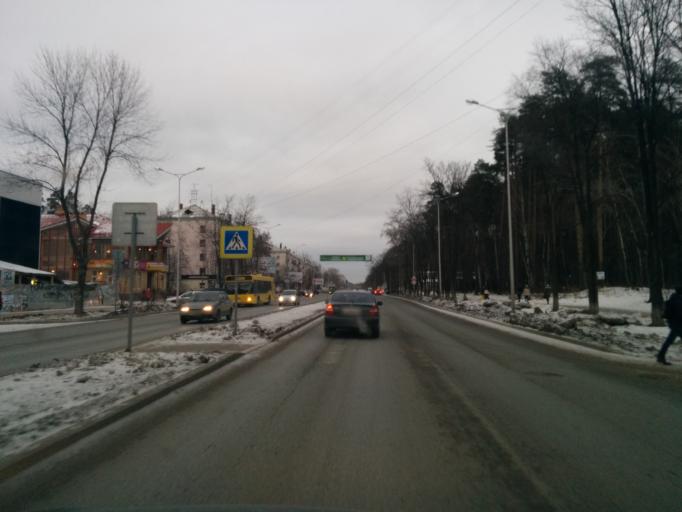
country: RU
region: Perm
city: Kultayevo
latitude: 58.0103
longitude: 55.9663
